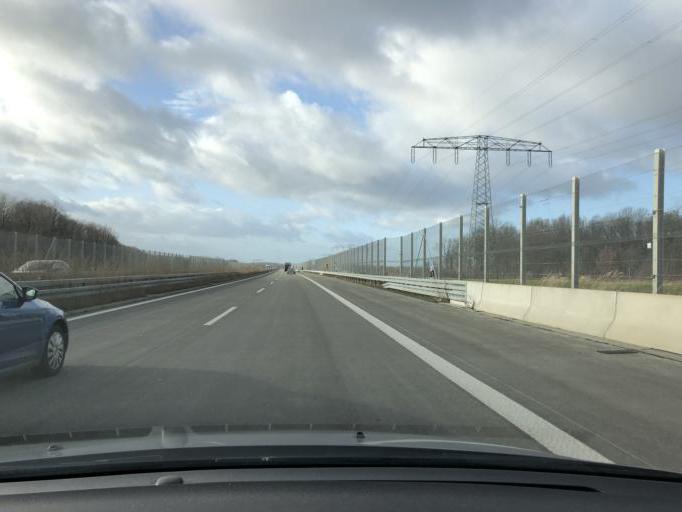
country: DE
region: Saxony
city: Frohburg
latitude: 51.0777
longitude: 12.5825
